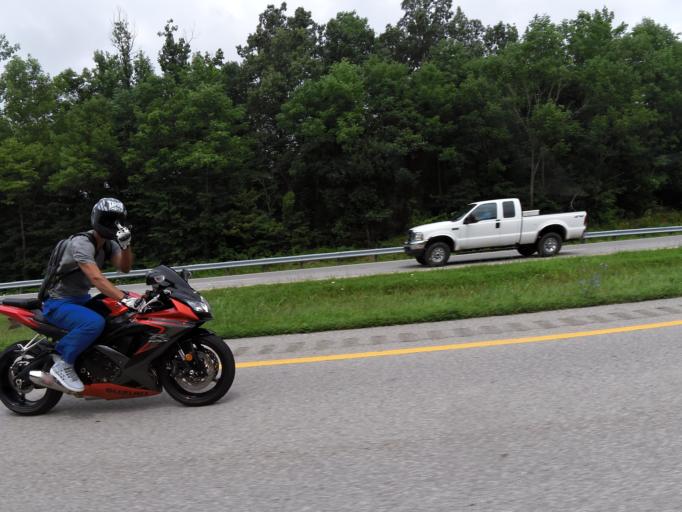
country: US
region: Kentucky
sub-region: Ohio County
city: Beaver Dam
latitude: 37.3271
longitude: -86.9894
